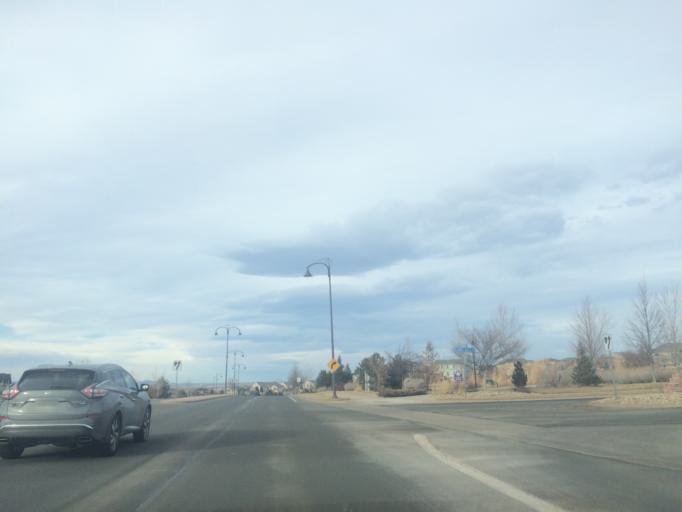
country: US
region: Colorado
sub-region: Boulder County
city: Lafayette
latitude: 39.9659
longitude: -105.0468
